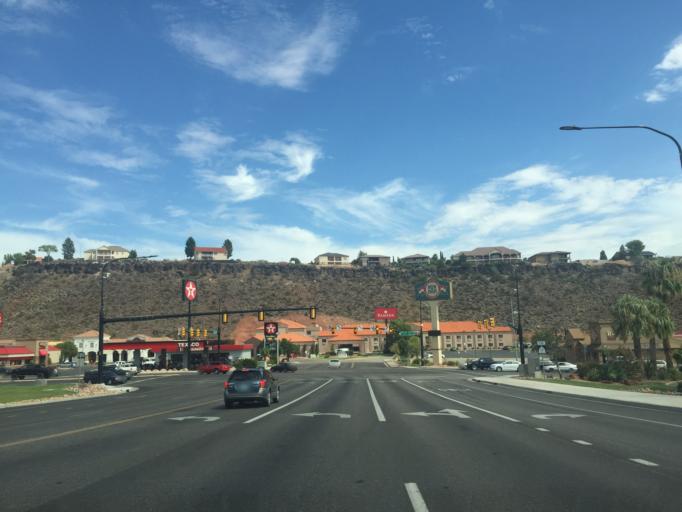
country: US
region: Utah
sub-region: Washington County
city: Saint George
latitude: 37.1097
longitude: -113.5555
